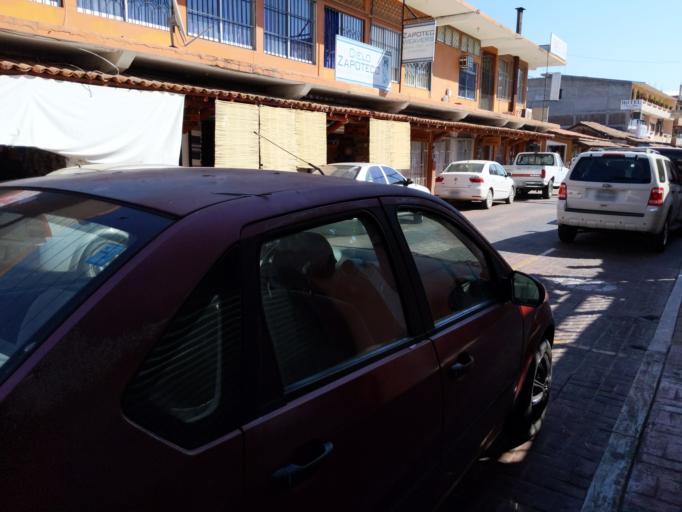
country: MX
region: Guerrero
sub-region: Zihuatanejo de Azueta
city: Ixtapa-Zihuatanejo
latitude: 17.6381
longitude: -101.5588
